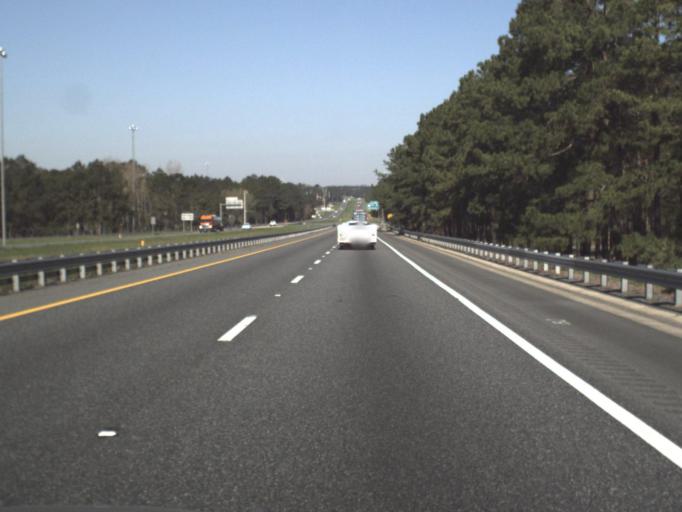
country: US
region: Florida
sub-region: Leon County
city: Tallahassee
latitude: 30.4835
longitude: -84.1555
